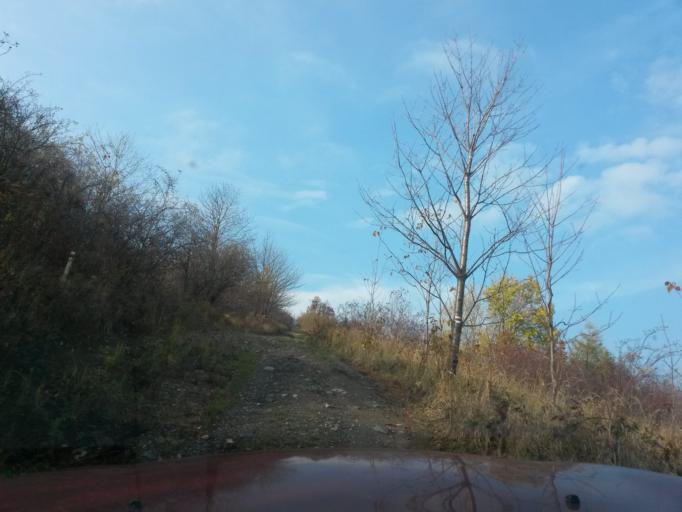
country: SK
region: Kosicky
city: Kosice
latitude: 48.7618
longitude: 21.2122
